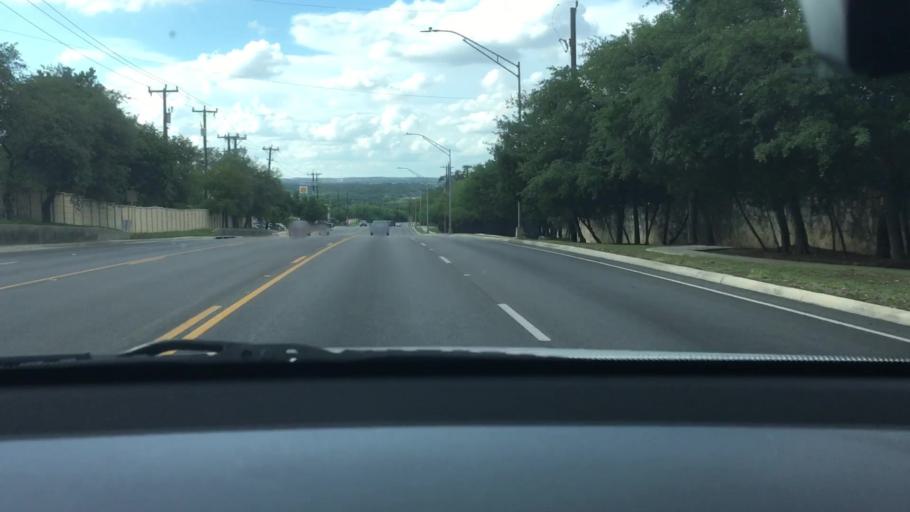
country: US
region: Texas
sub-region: Bexar County
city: Live Oak
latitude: 29.5956
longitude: -98.4024
